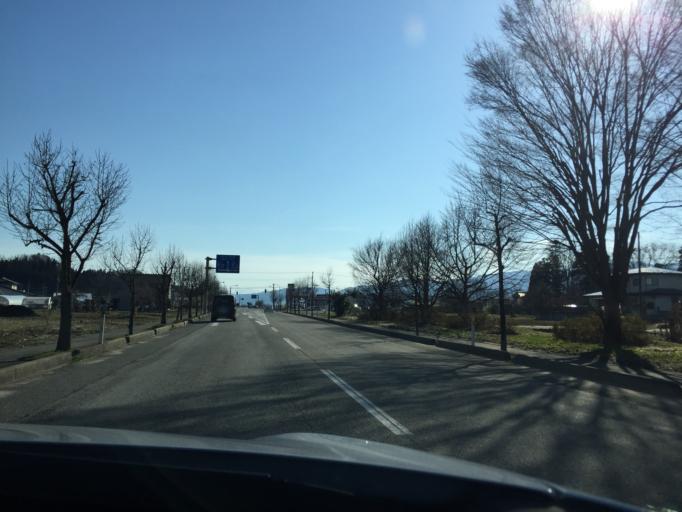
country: JP
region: Yamagata
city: Nagai
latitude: 38.1588
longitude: 140.0734
